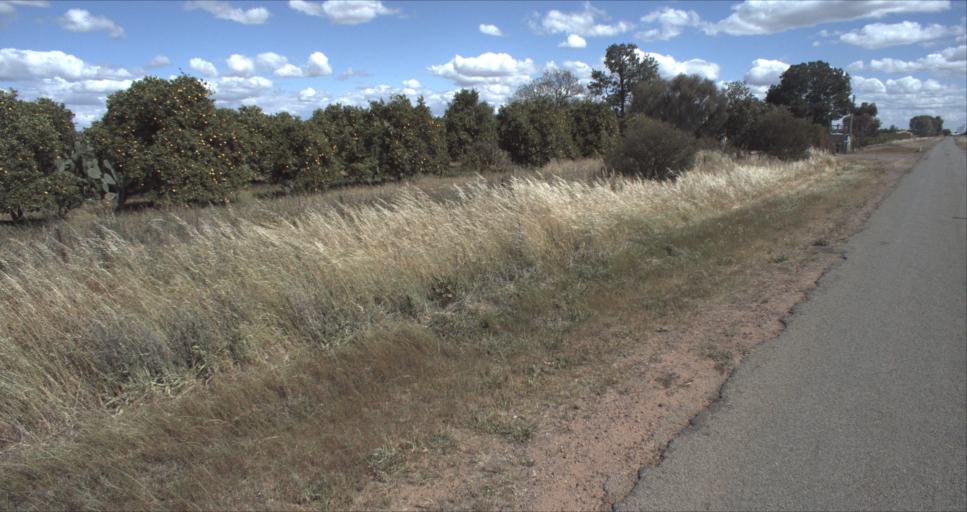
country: AU
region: New South Wales
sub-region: Leeton
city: Leeton
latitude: -34.5130
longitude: 146.2414
